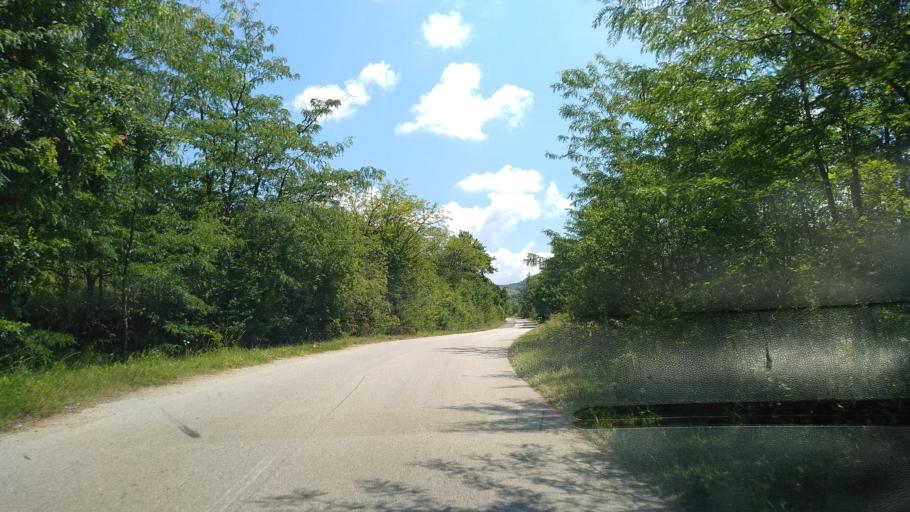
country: RO
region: Hunedoara
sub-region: Comuna Bosorod
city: Bosorod
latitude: 45.7002
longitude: 23.0849
